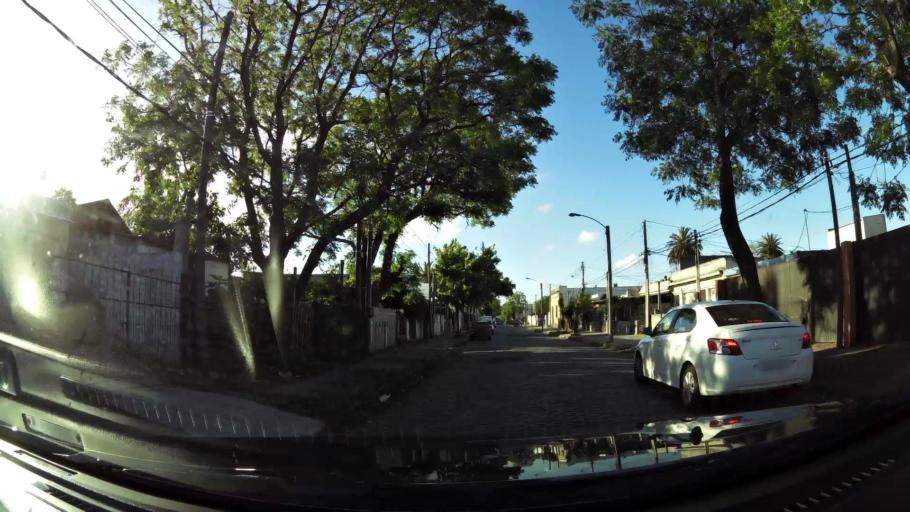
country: UY
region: Montevideo
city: Montevideo
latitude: -34.8696
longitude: -56.1467
